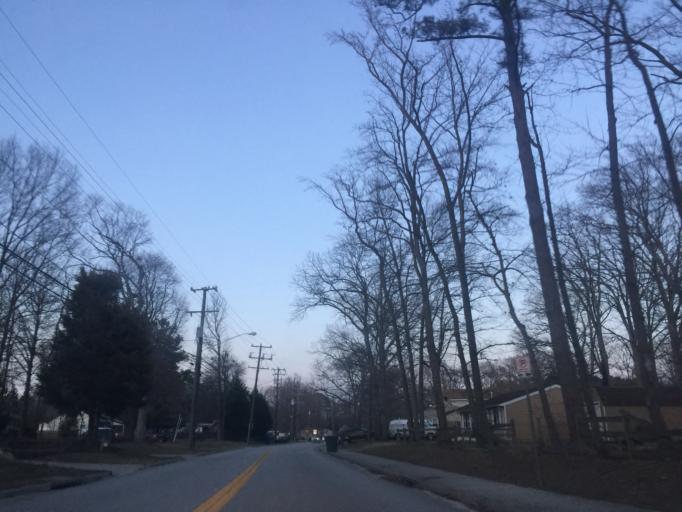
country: US
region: Virginia
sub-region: City of Newport News
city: Newport News
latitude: 37.0771
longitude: -76.5034
